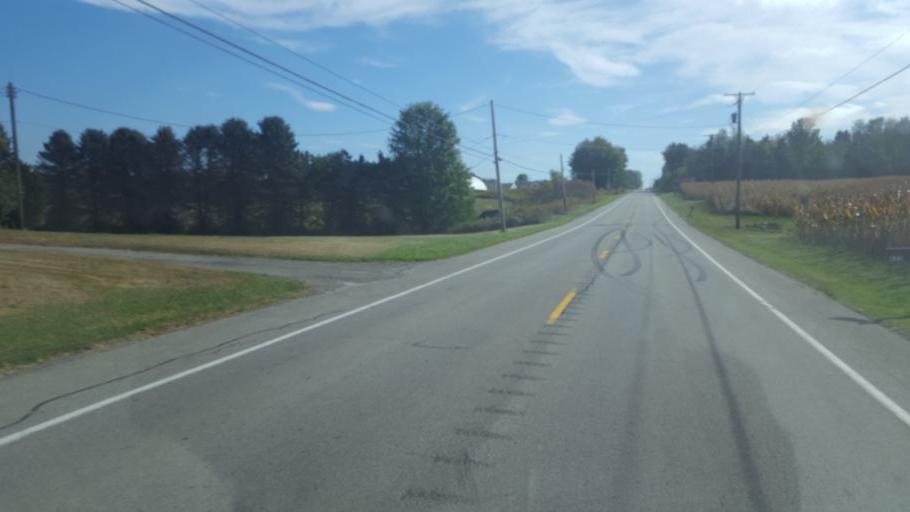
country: US
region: Pennsylvania
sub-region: Mercer County
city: Mercer
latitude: 41.2641
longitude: -80.2389
